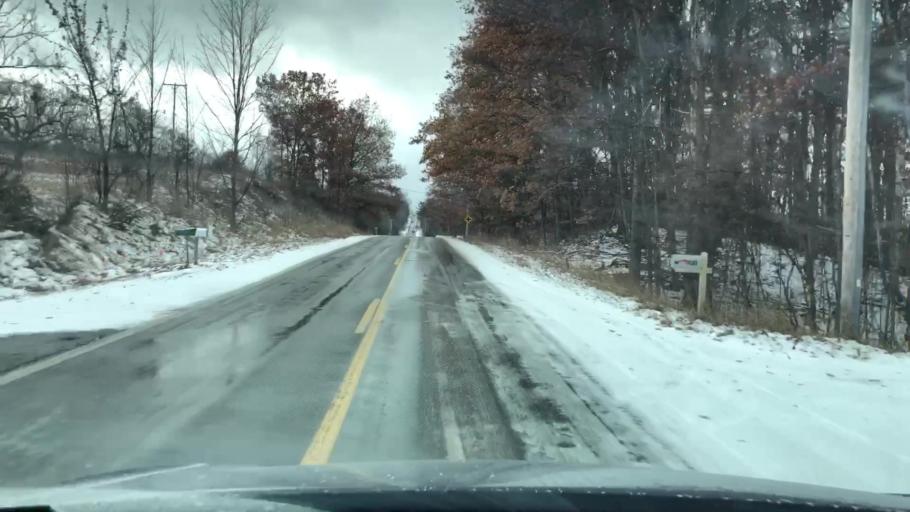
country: US
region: Michigan
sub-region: Antrim County
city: Elk Rapids
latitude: 44.8957
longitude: -85.5154
